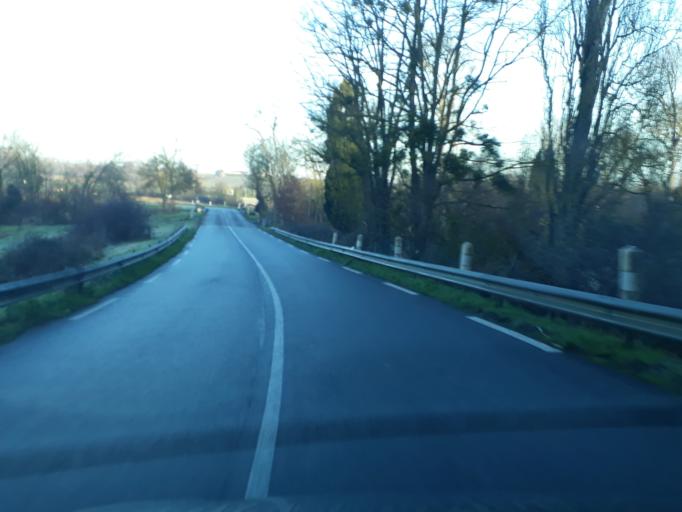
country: FR
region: Midi-Pyrenees
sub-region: Departement de la Haute-Garonne
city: Berat
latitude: 43.3833
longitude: 1.1749
